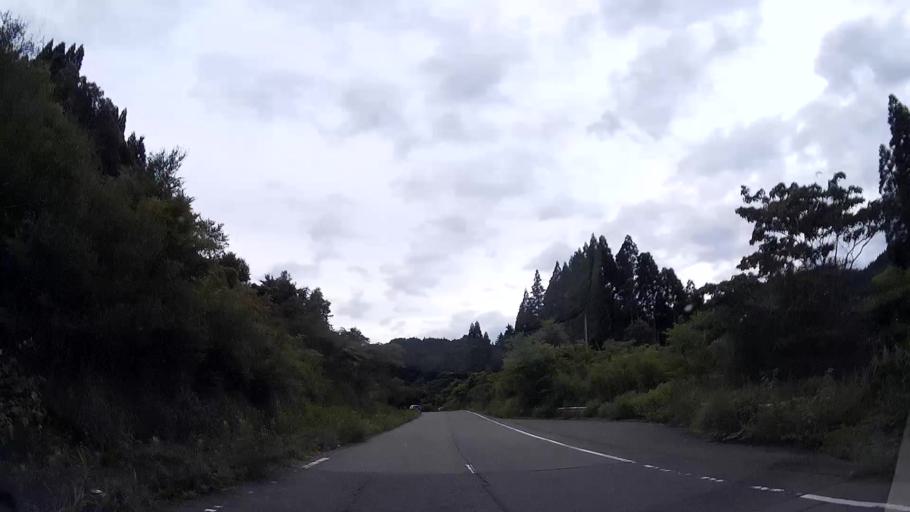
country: JP
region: Oita
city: Hita
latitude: 33.1361
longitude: 130.9860
